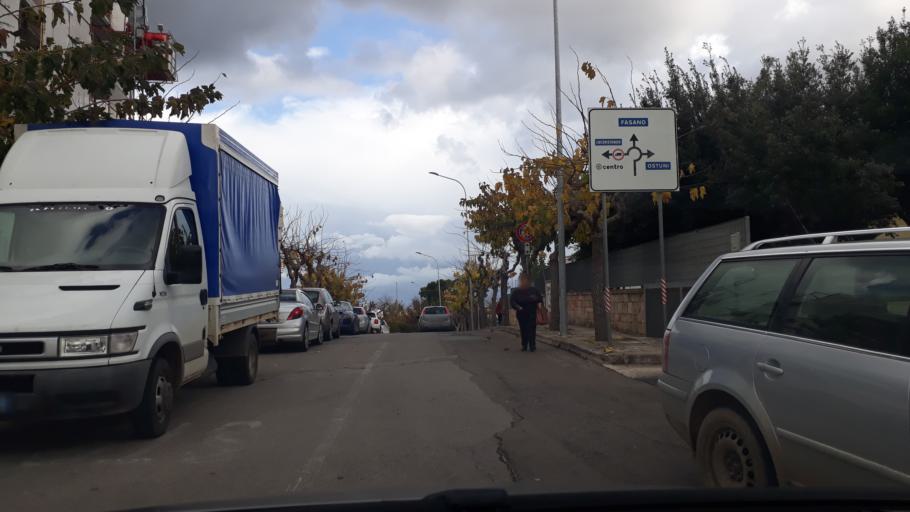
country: IT
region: Apulia
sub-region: Provincia di Brindisi
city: Cisternino
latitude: 40.7402
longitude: 17.4314
